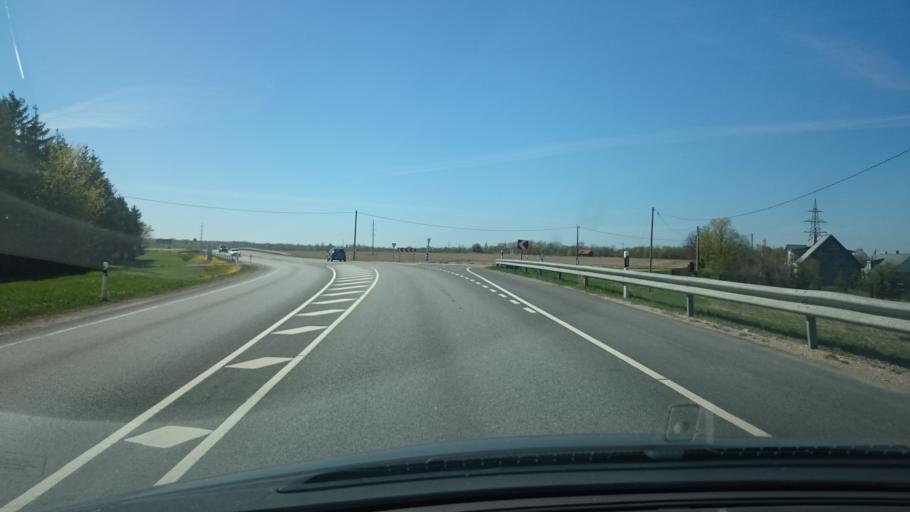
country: EE
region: Ida-Virumaa
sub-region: Narva-Joesuu linn
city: Narva-Joesuu
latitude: 59.4070
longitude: 28.0319
